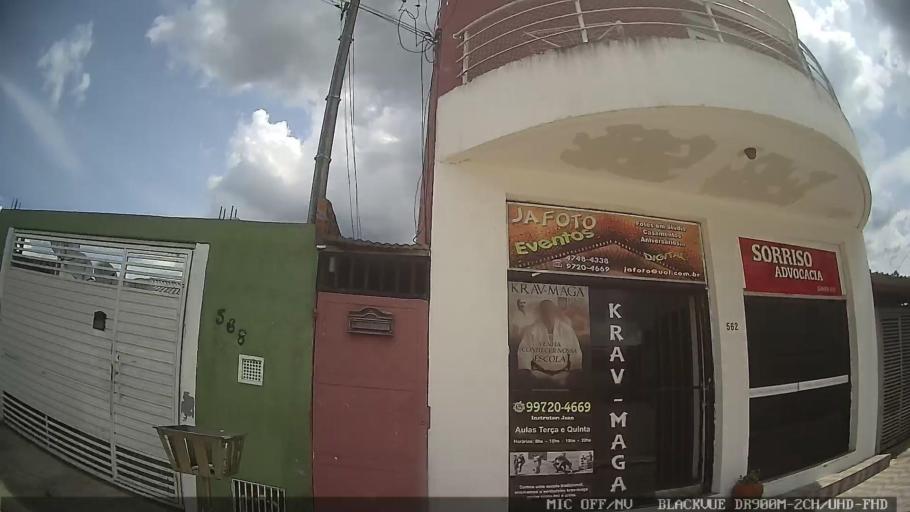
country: BR
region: Sao Paulo
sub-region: Suzano
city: Suzano
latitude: -23.5400
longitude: -46.3043
